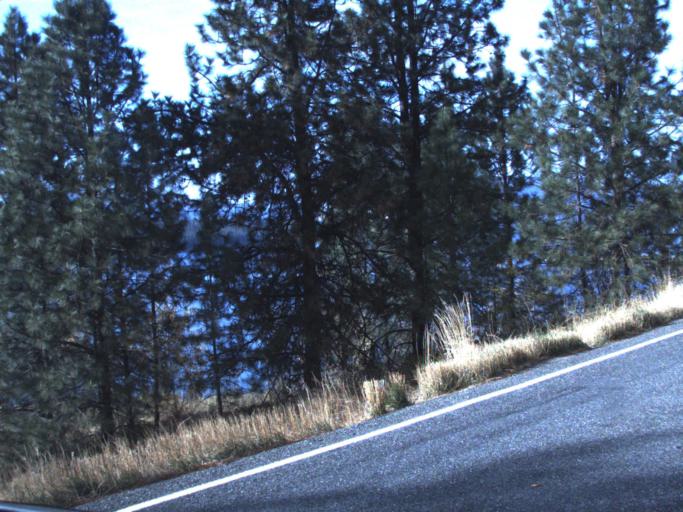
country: US
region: Washington
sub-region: Stevens County
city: Kettle Falls
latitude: 48.2750
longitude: -118.1349
